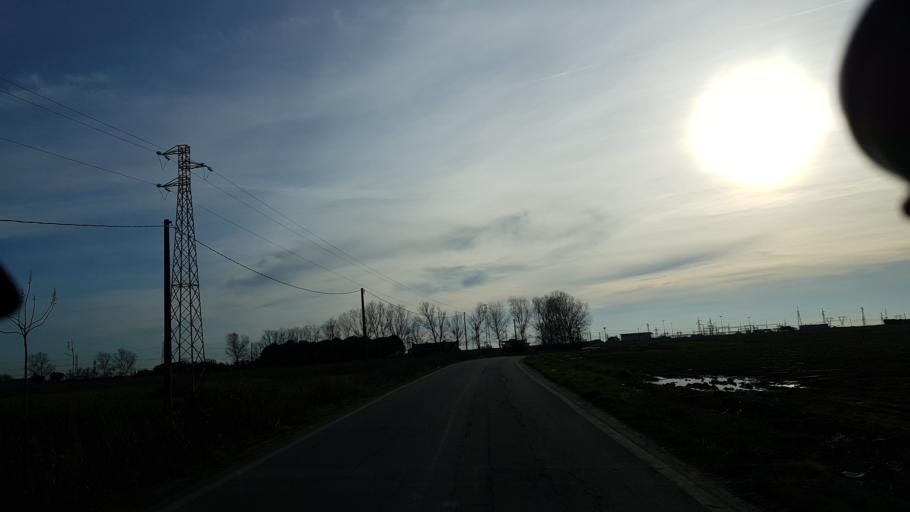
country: IT
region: Apulia
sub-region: Provincia di Brindisi
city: Brindisi
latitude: 40.6096
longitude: 17.9130
